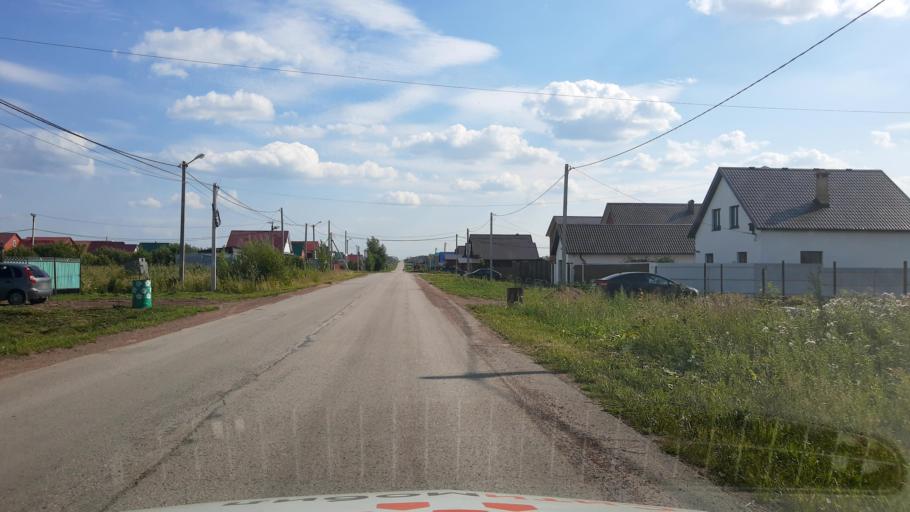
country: RU
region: Bashkortostan
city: Kabakovo
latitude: 54.6621
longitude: 56.2139
